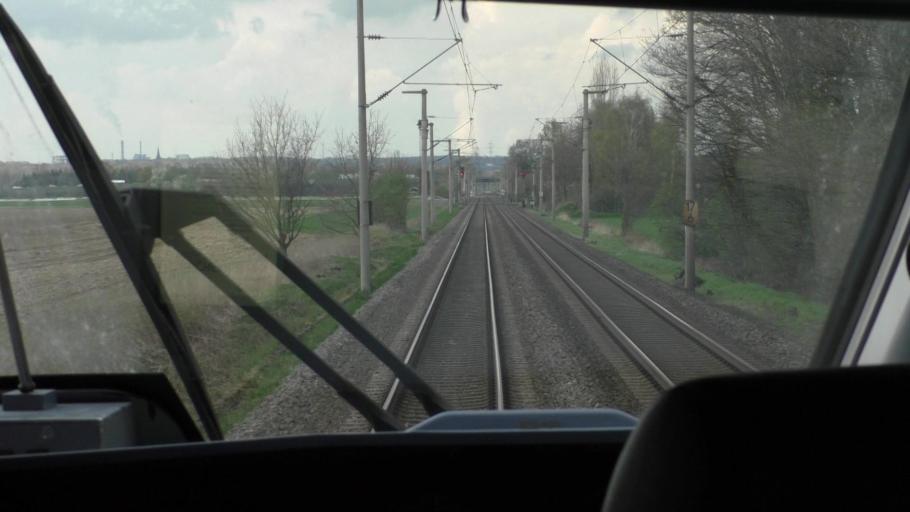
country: DE
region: North Rhine-Westphalia
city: Wesseling
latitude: 50.8074
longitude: 6.9407
